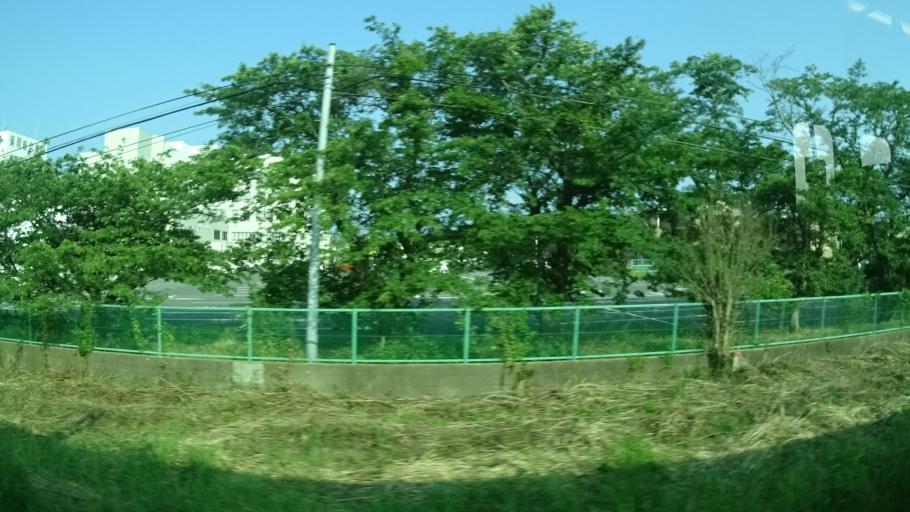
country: JP
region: Ibaraki
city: Kitaibaraki
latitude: 36.8997
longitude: 140.7813
